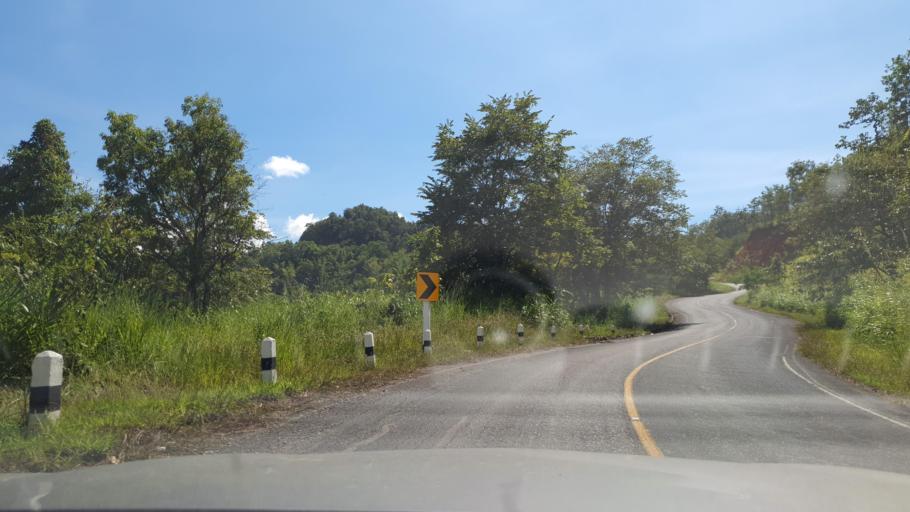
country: TH
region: Chiang Mai
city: Phrao
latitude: 19.3604
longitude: 99.2752
